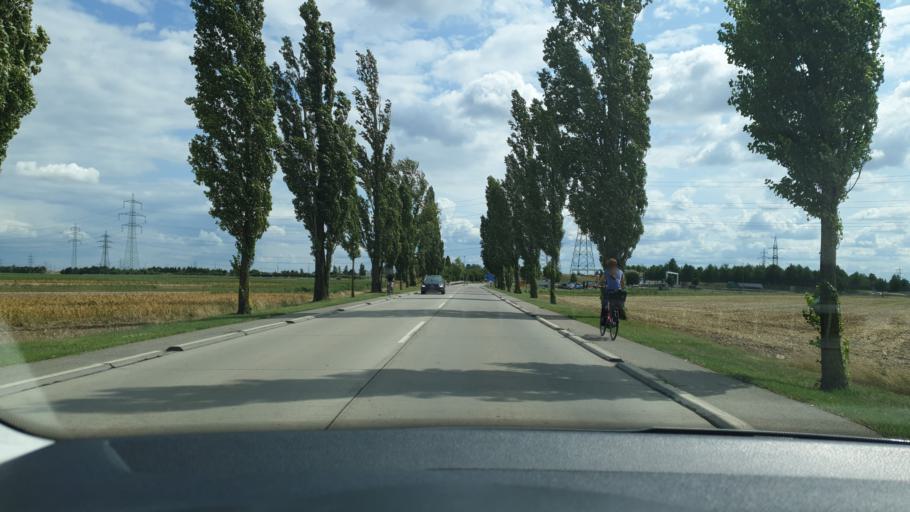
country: AT
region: Lower Austria
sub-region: Politischer Bezirk Wien-Umgebung
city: Leopoldsdorf
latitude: 48.1308
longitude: 16.3869
